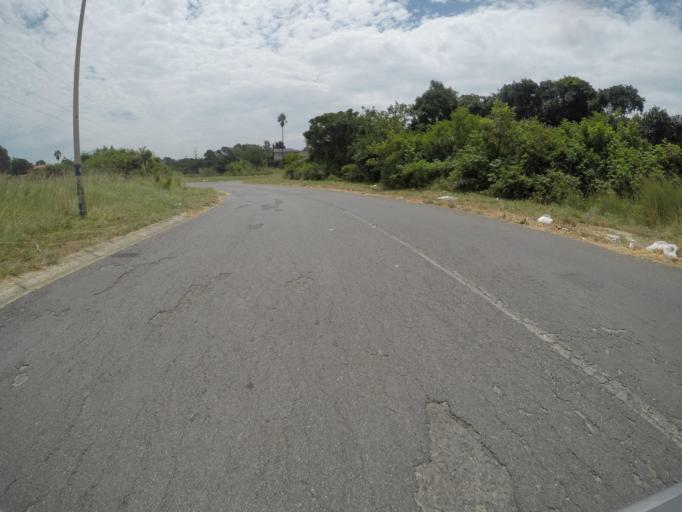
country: ZA
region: Eastern Cape
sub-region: Buffalo City Metropolitan Municipality
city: East London
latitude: -32.9818
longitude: 27.8703
